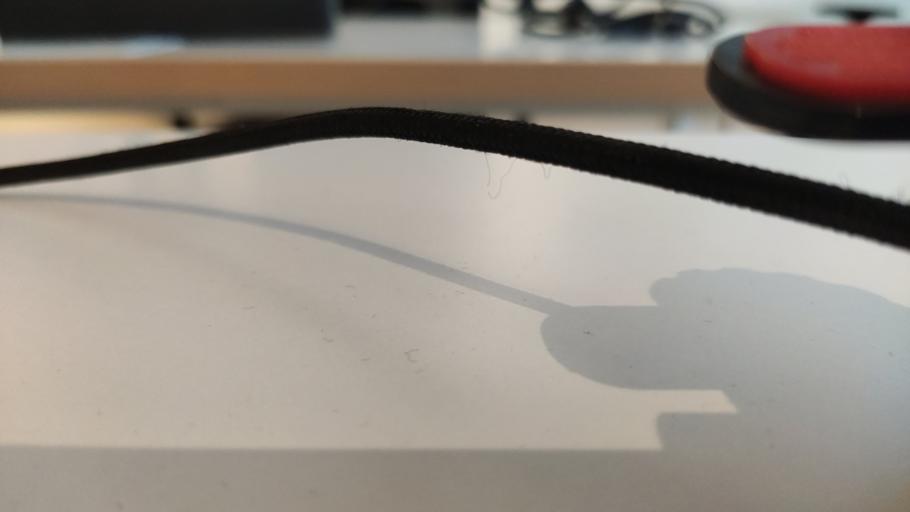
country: RU
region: Moskovskaya
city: Novopetrovskoye
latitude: 55.9246
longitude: 36.4358
